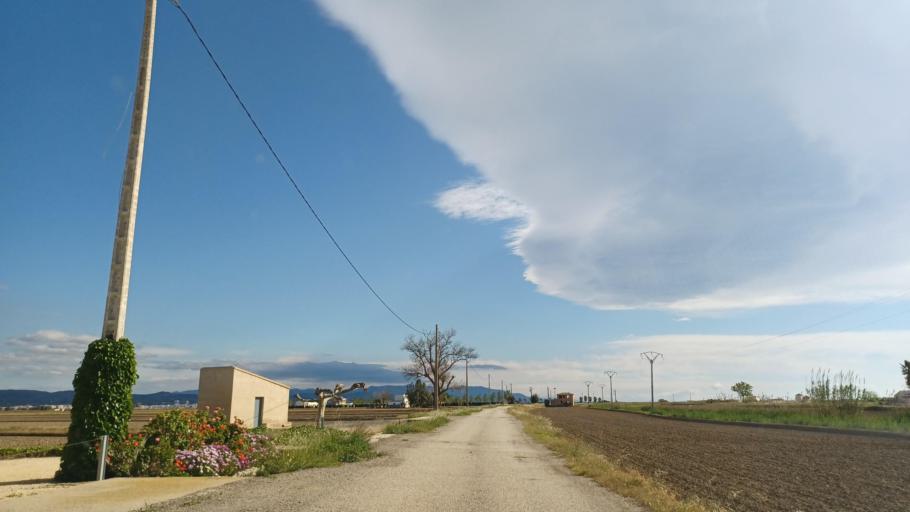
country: ES
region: Catalonia
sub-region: Provincia de Tarragona
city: L'Ampolla
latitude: 40.7729
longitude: 0.7098
